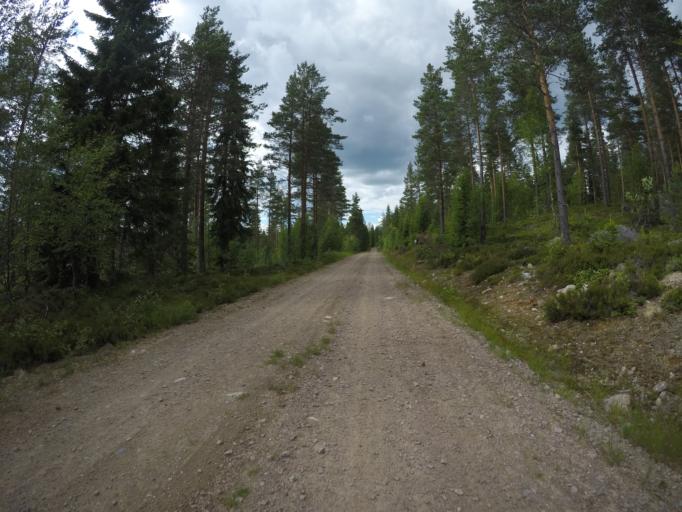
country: SE
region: Vaermland
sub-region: Filipstads Kommun
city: Lesjofors
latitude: 60.0782
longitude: 14.4381
